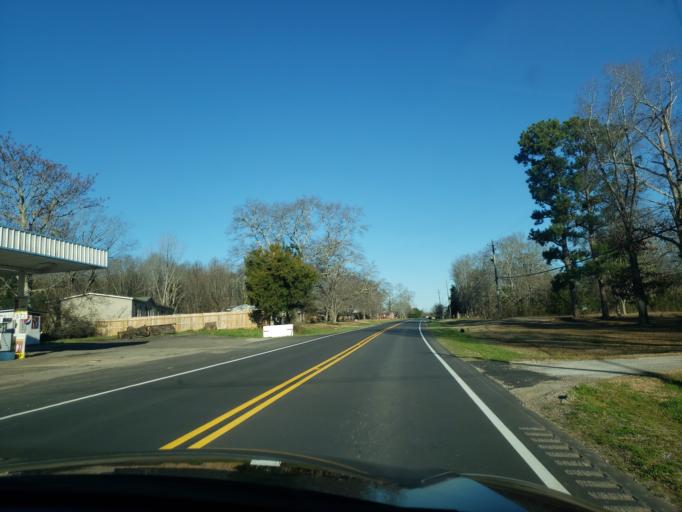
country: US
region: Alabama
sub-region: Macon County
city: Tuskegee
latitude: 32.5662
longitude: -85.6831
